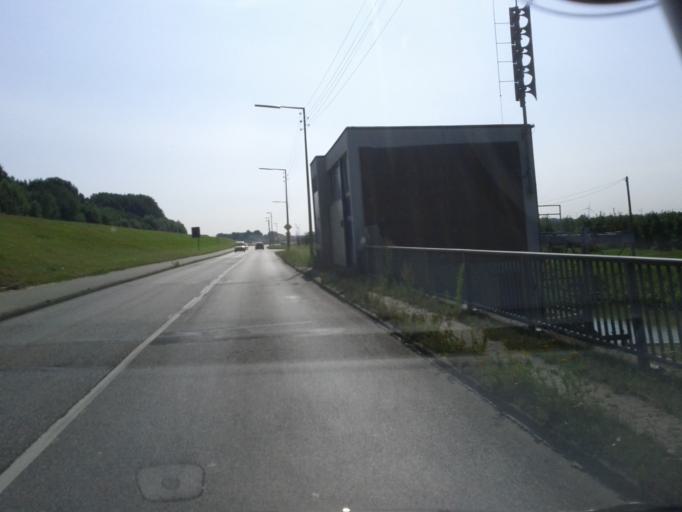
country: DE
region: Lower Saxony
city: Neu Wulmstorf
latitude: 53.5298
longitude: 9.8062
